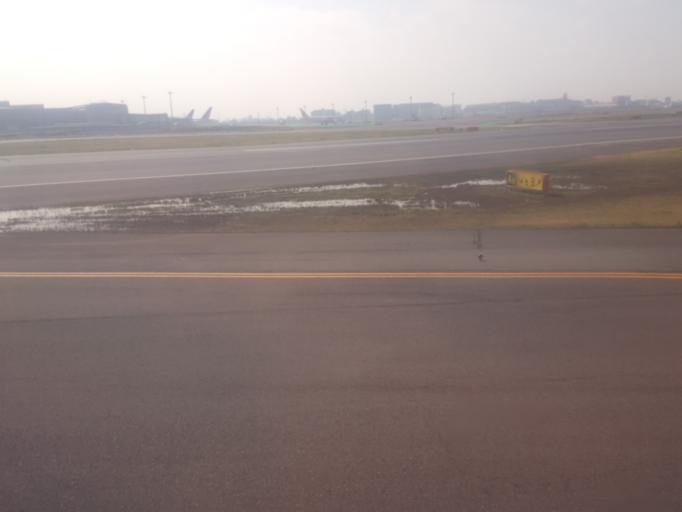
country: JP
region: Kanagawa
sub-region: Kawasaki-shi
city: Kawasaki
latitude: 35.5512
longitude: 139.7762
